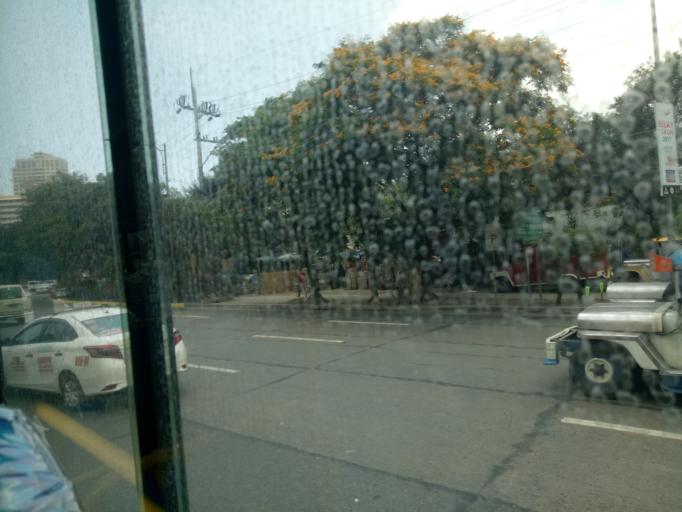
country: PH
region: Metro Manila
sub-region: Quezon City
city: Quezon City
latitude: 14.6492
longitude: 121.0479
